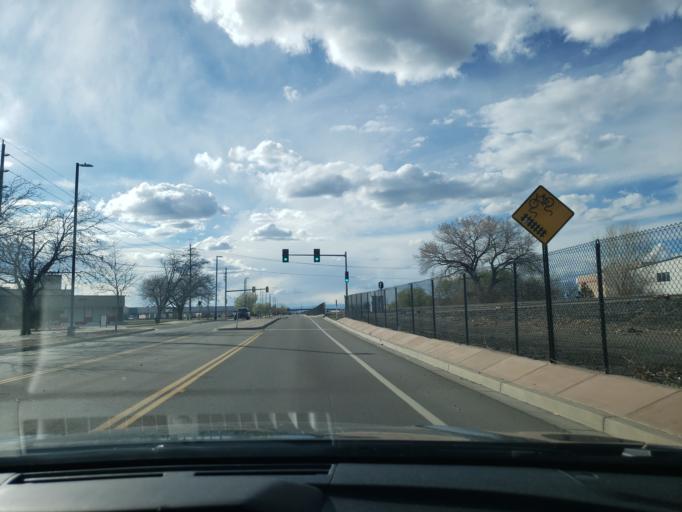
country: US
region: Colorado
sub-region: Mesa County
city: Redlands
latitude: 39.0851
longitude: -108.5975
